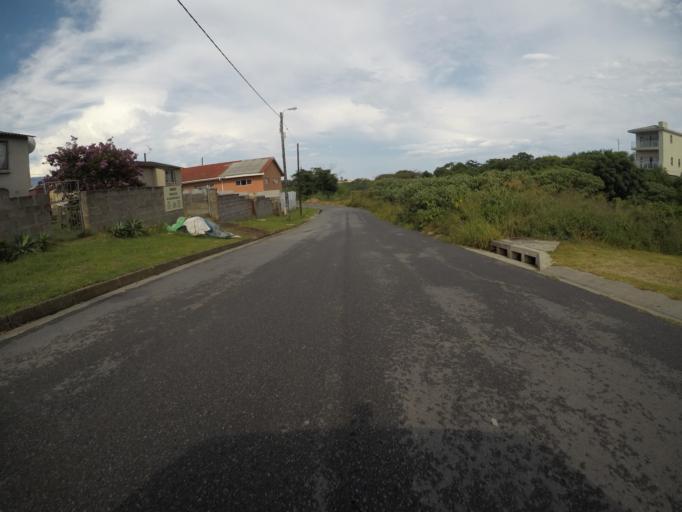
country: ZA
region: Eastern Cape
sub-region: Buffalo City Metropolitan Municipality
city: East London
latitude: -33.0234
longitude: 27.8765
